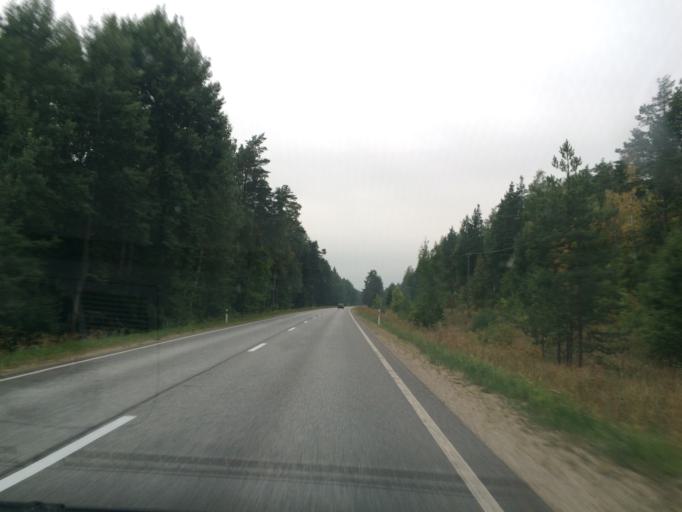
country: LV
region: Varaklani
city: Varaklani
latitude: 56.5386
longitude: 26.5641
